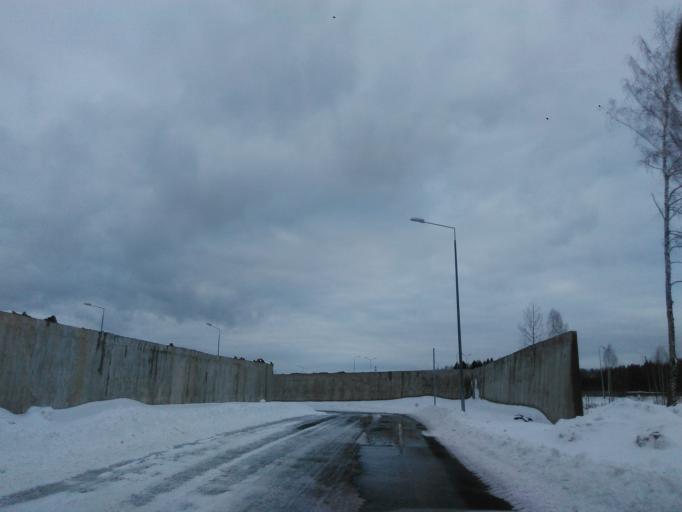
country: RU
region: Moskovskaya
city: Rzhavki
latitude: 56.0018
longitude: 37.2589
